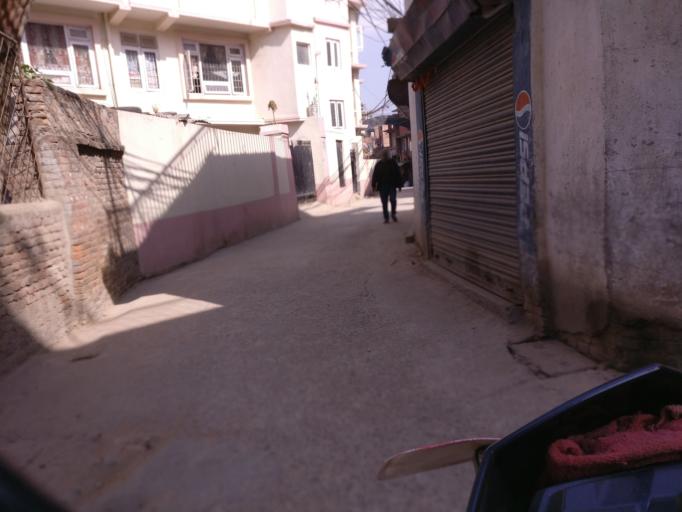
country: NP
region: Central Region
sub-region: Bagmati Zone
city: Patan
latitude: 27.6666
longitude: 85.3295
